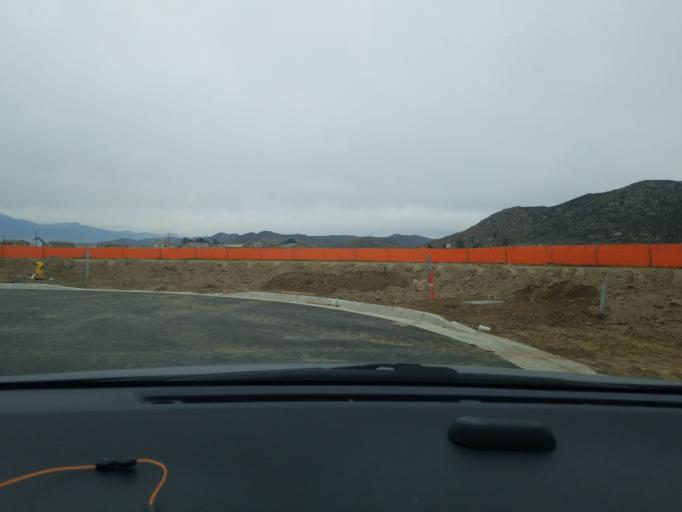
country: US
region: California
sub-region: Riverside County
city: Winchester
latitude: 33.6939
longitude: -117.1000
